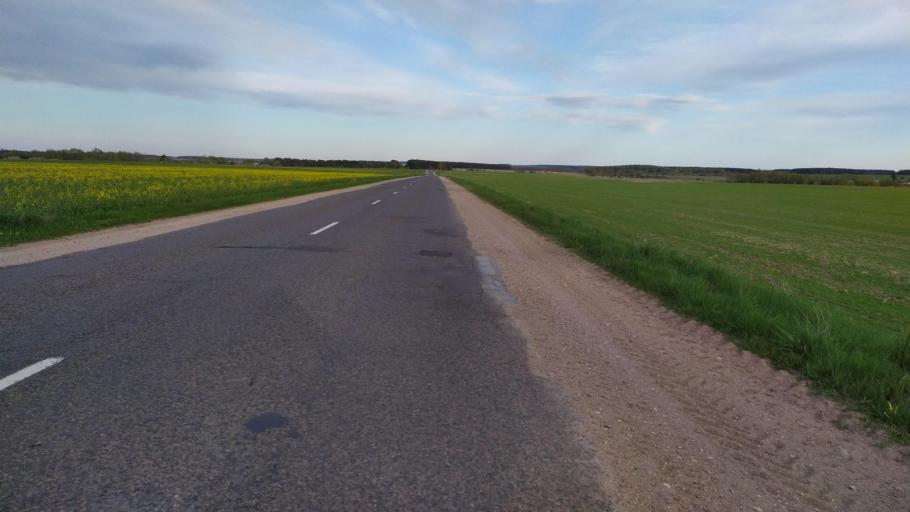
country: BY
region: Brest
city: Kamyanyets
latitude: 52.4143
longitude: 23.7101
